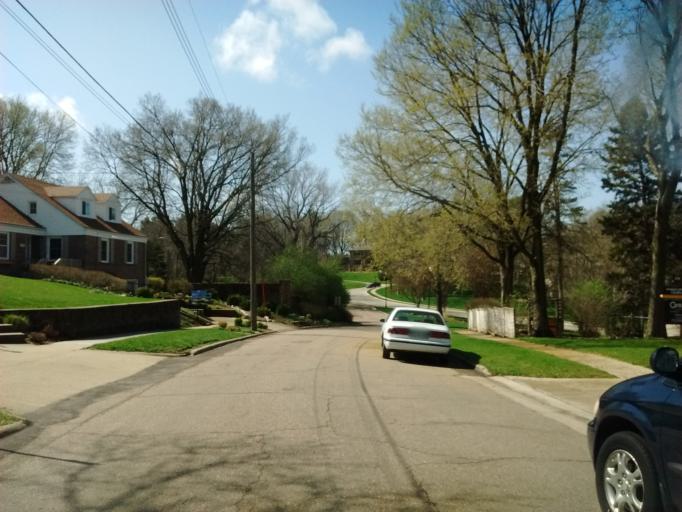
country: US
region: Iowa
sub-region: Woodbury County
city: Sioux City
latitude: 42.5200
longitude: -96.4113
